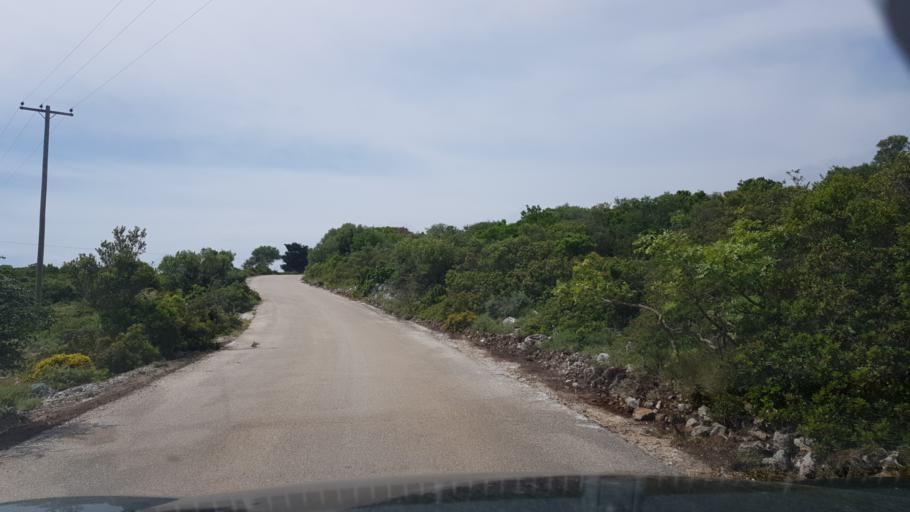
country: GR
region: Ionian Islands
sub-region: Lefkada
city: Nidri
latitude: 38.6099
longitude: 20.5658
